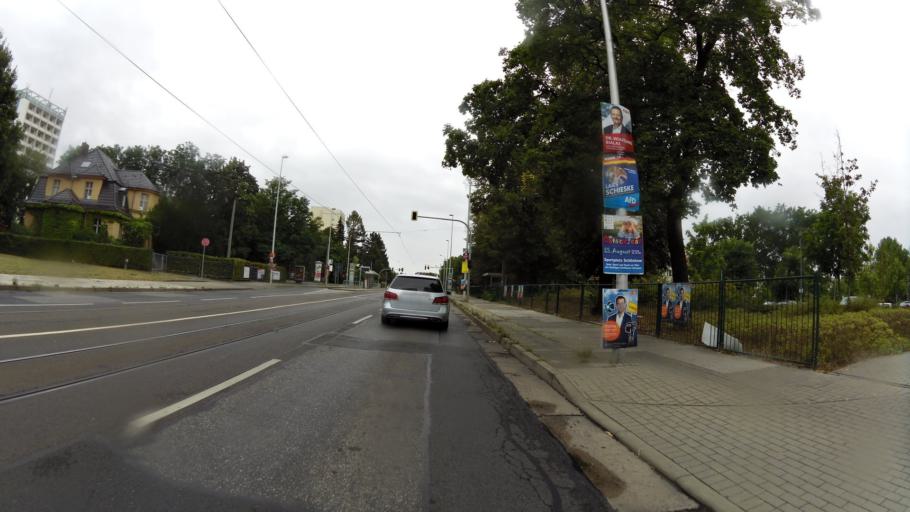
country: DE
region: Brandenburg
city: Cottbus
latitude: 51.7415
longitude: 14.3247
